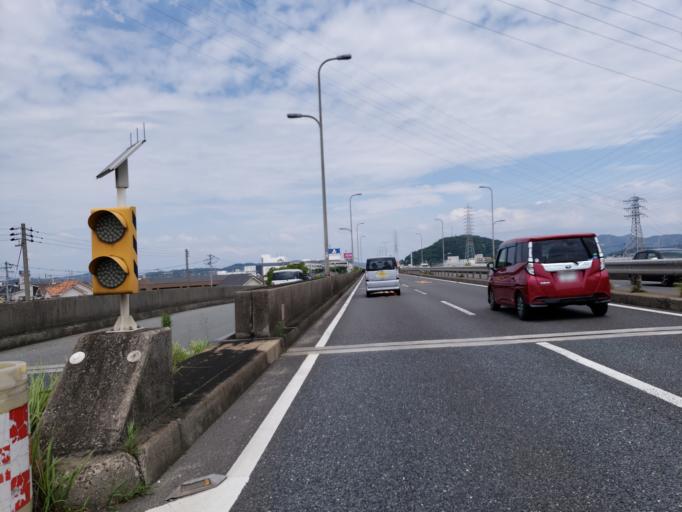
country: JP
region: Hyogo
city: Kakogawacho-honmachi
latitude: 34.7669
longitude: 134.8075
